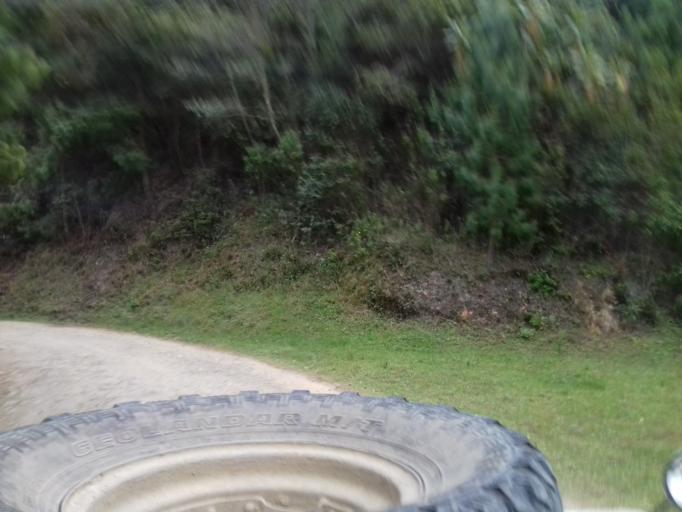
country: CO
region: Quindio
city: Salento
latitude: 4.5893
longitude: -75.5233
